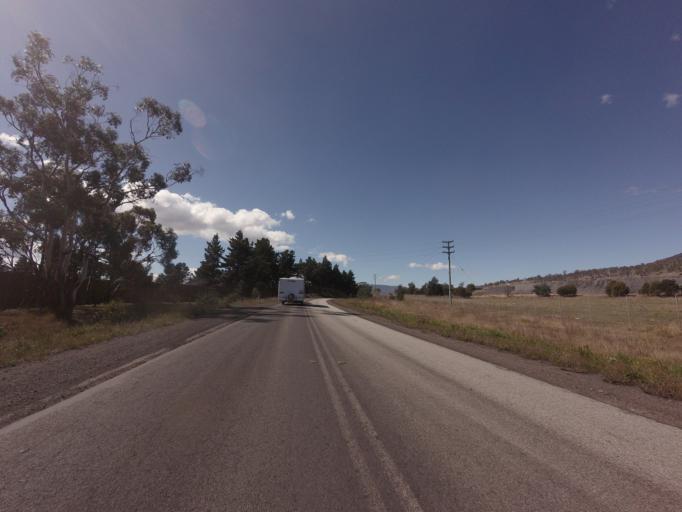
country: AU
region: Tasmania
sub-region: Break O'Day
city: St Helens
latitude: -41.6309
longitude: 147.9859
